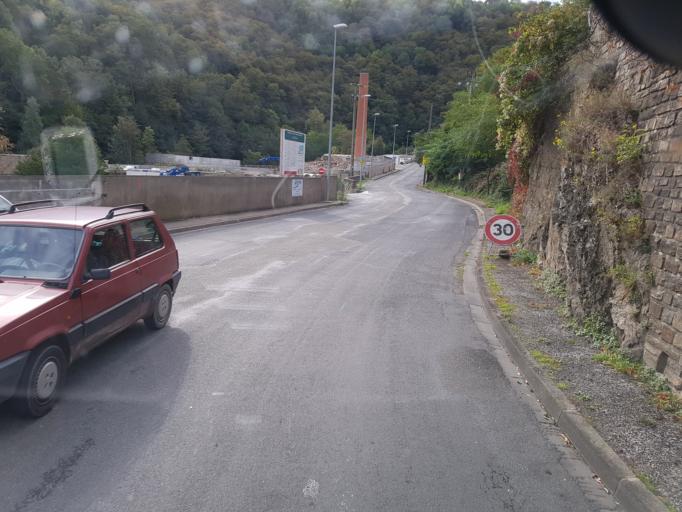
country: FR
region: Midi-Pyrenees
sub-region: Departement du Tarn
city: Mazamet
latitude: 43.4826
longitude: 2.3759
